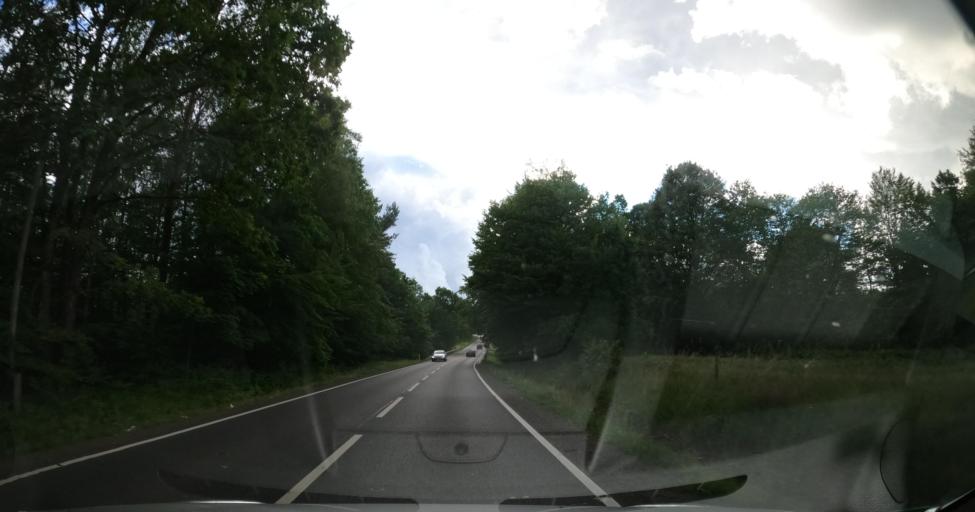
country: PL
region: Pomeranian Voivodeship
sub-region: Powiat bytowski
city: Czarna Dabrowka
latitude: 54.3393
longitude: 17.6286
